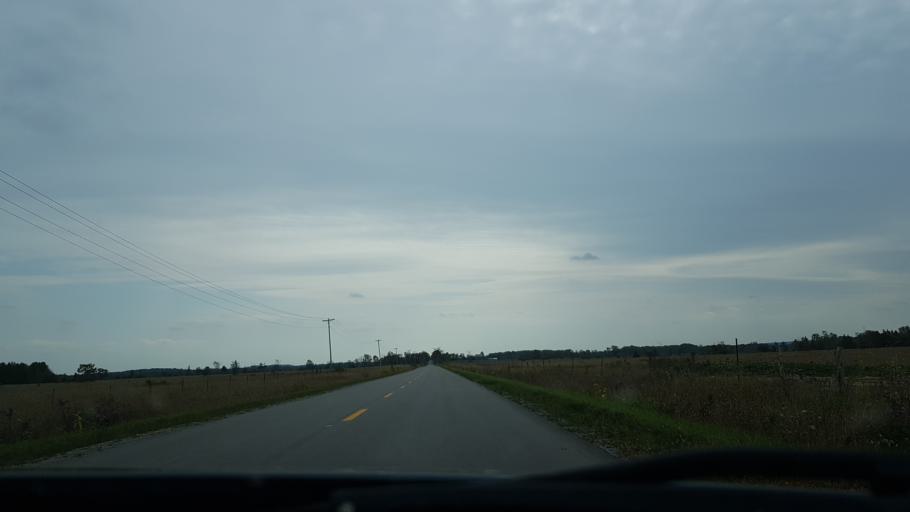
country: CA
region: Ontario
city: Orillia
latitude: 44.6379
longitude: -78.9591
